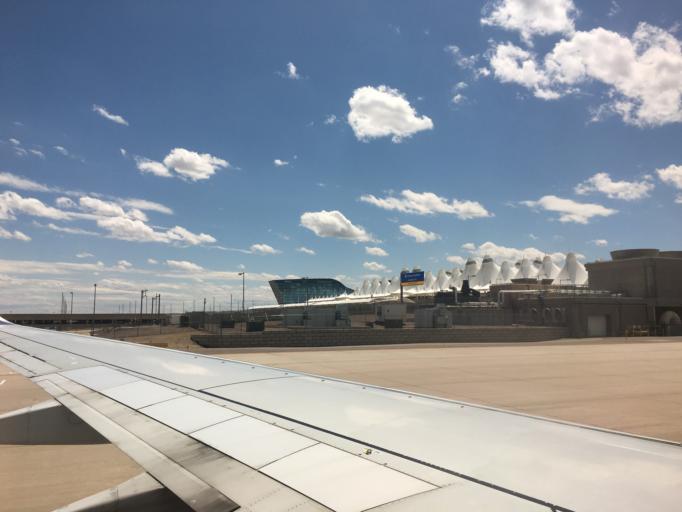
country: US
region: Colorado
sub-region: Weld County
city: Lochbuie
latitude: 39.8528
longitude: -104.6704
